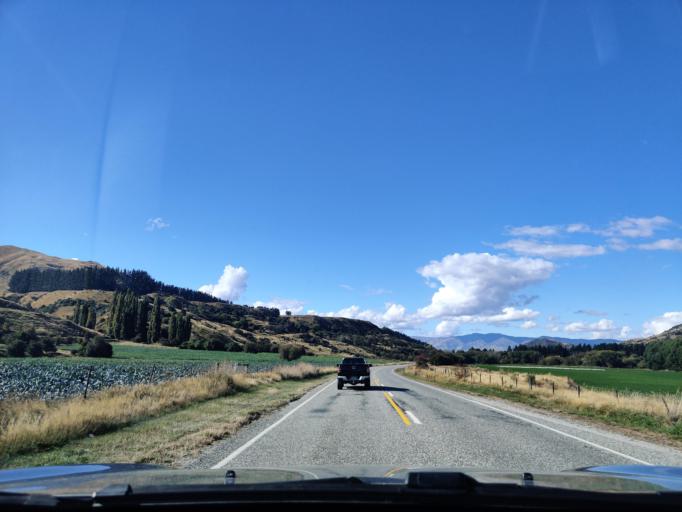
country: NZ
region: Otago
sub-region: Queenstown-Lakes District
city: Wanaka
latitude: -44.7572
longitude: 169.1048
